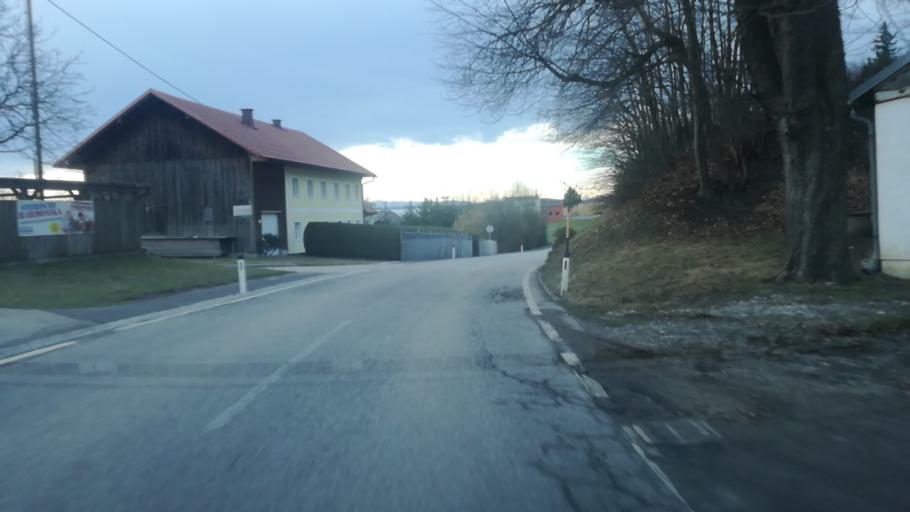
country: AT
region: Upper Austria
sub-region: Politischer Bezirk Ried im Innkreis
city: Waldzell
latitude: 48.1786
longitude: 13.4437
